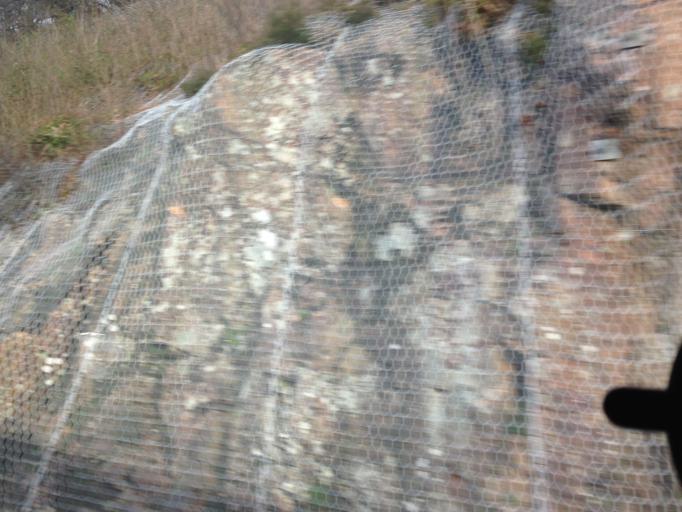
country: GB
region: Scotland
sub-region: Argyll and Bute
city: Garelochhead
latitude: 56.1667
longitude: -4.7817
